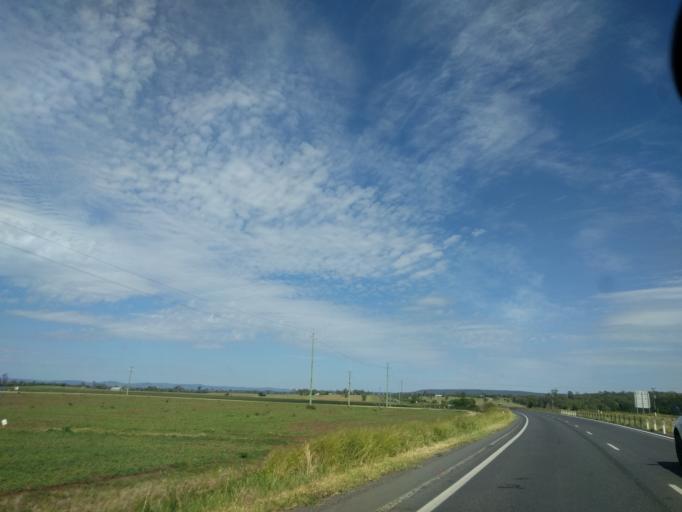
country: AU
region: Queensland
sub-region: Lockyer Valley
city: Gatton
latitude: -27.5437
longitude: 152.3080
